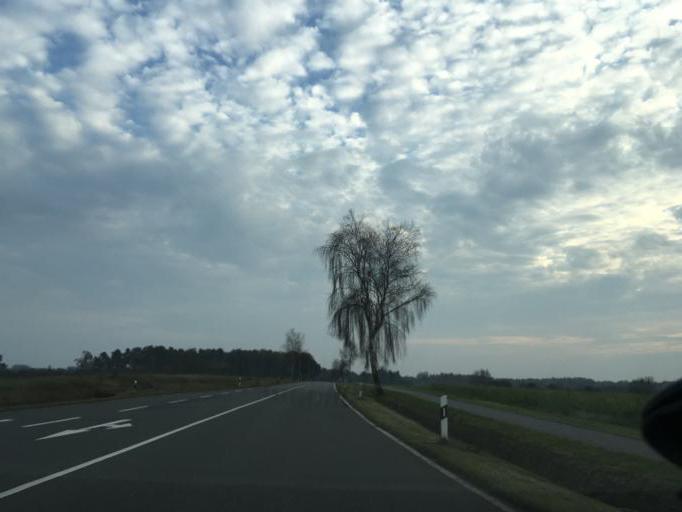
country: DE
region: Lower Saxony
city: Wietzendorf
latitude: 52.9607
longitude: 9.9732
